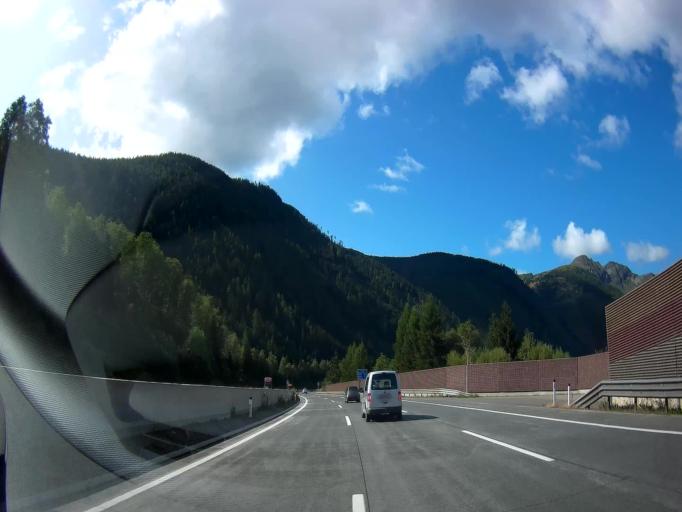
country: AT
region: Salzburg
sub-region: Politischer Bezirk Tamsweg
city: Sankt Michael im Lungau
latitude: 47.0880
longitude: 13.6069
